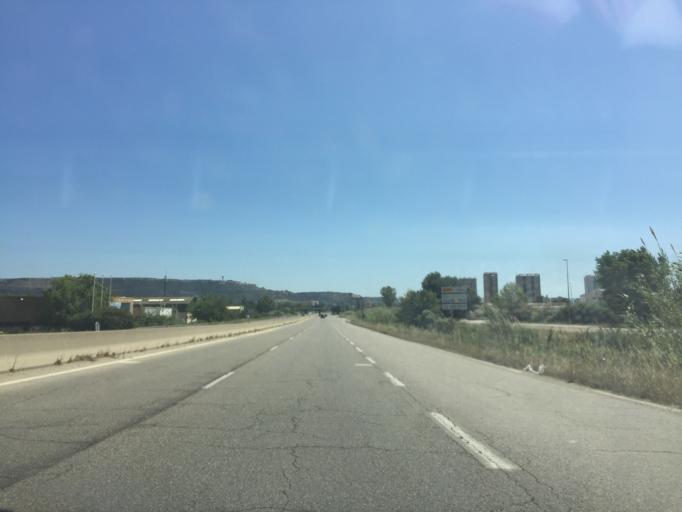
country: FR
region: Provence-Alpes-Cote d'Azur
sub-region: Departement des Bouches-du-Rhone
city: Rognac
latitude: 43.4987
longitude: 5.2137
